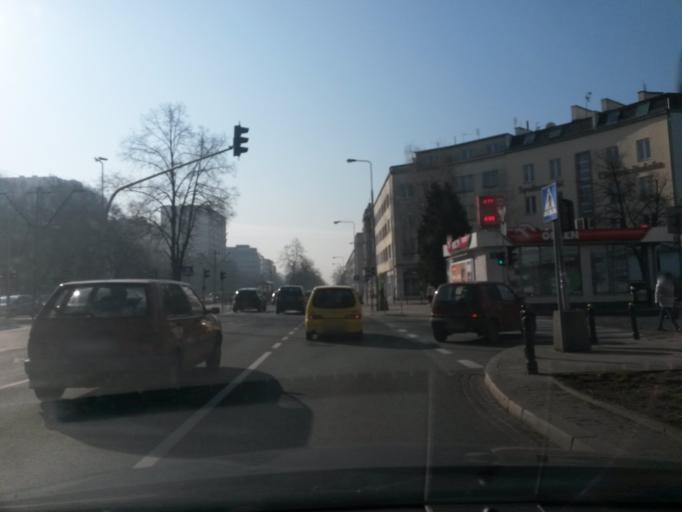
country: PL
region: Masovian Voivodeship
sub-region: Warszawa
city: Mokotow
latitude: 52.1949
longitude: 21.0241
